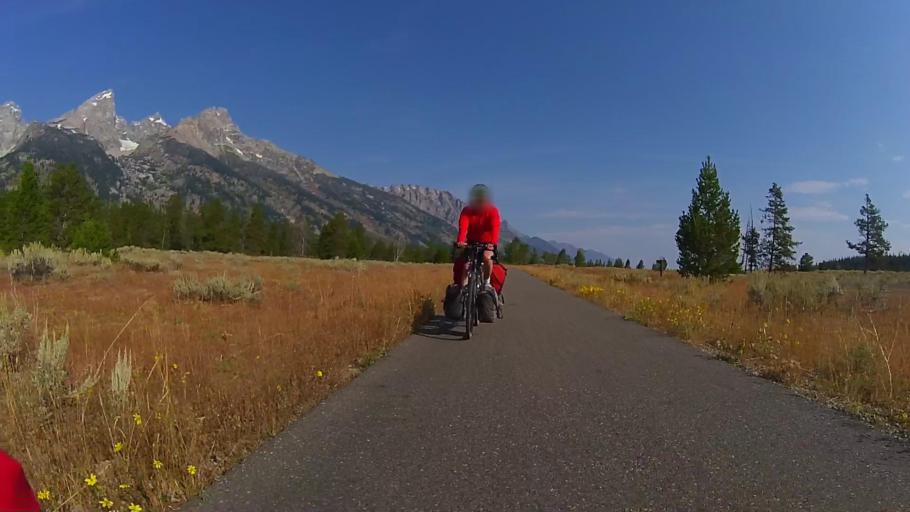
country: US
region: Wyoming
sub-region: Teton County
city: Moose Wilson Road
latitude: 43.7158
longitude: -110.7284
